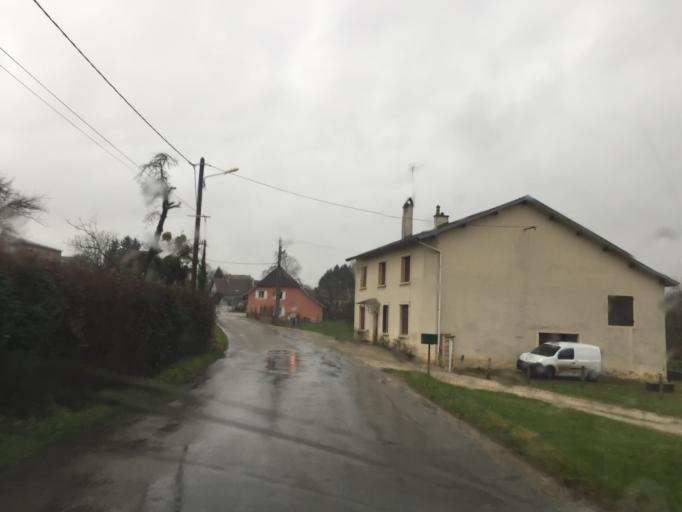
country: FR
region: Franche-Comte
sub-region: Departement du Doubs
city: Arc-et-Senans
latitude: 46.9990
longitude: 5.7613
